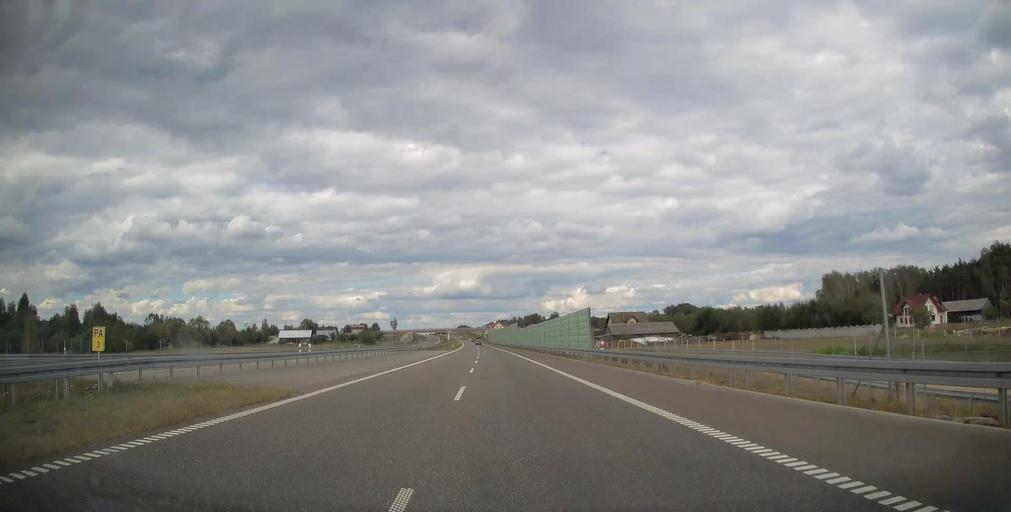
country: PL
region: Masovian Voivodeship
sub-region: Powiat radomski
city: Jedlinsk
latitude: 51.5043
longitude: 21.0806
